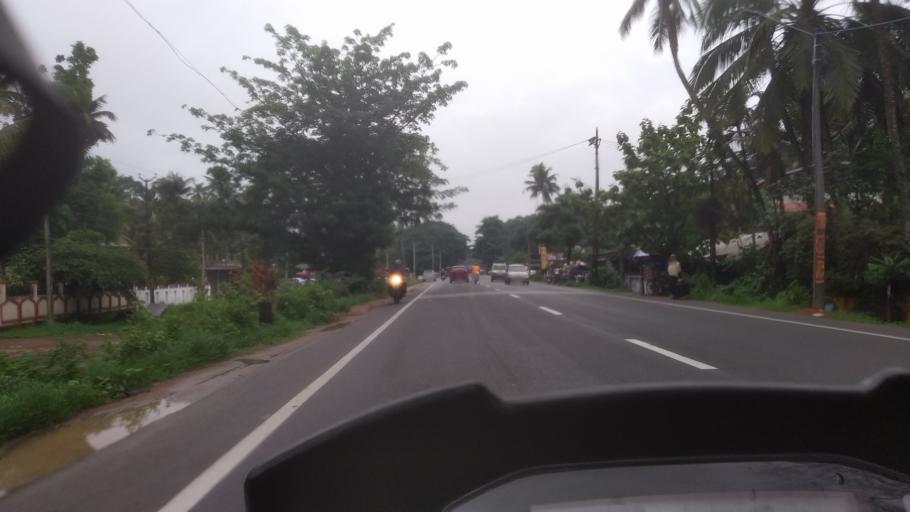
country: IN
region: Kerala
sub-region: Alappuzha
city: Kayankulam
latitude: 9.1856
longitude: 76.4895
